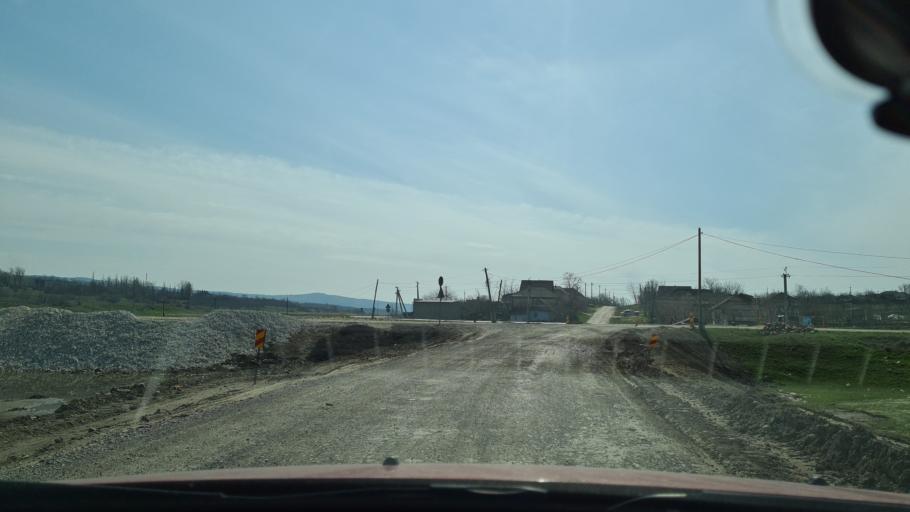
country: MD
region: Ungheni
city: Ungheni
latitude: 47.3207
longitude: 27.8954
